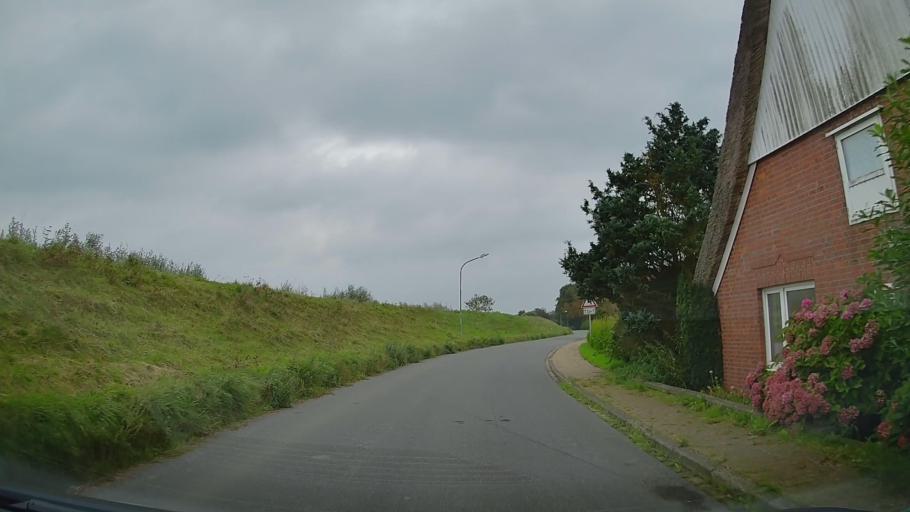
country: DE
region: Lower Saxony
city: Balje
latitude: 53.8316
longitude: 9.1355
